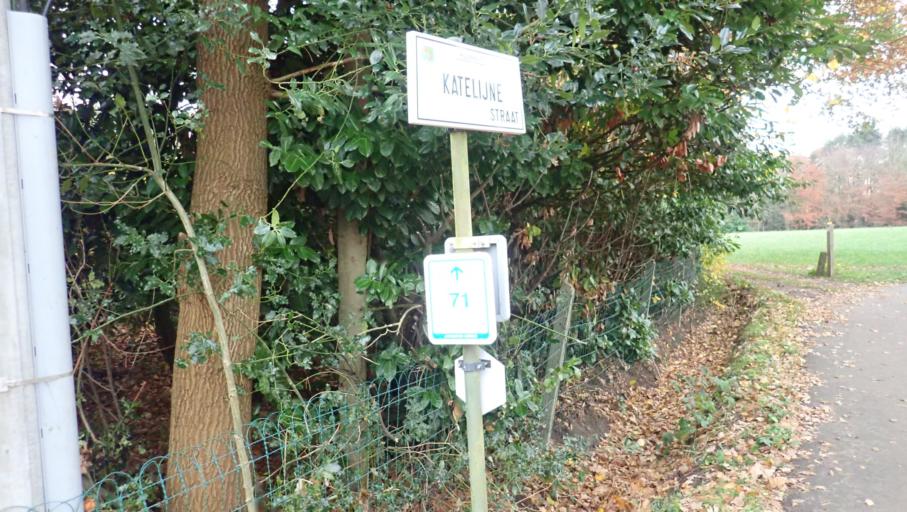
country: BE
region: Flanders
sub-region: Provincie Antwerpen
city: Hulshout
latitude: 51.0673
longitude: 4.8144
